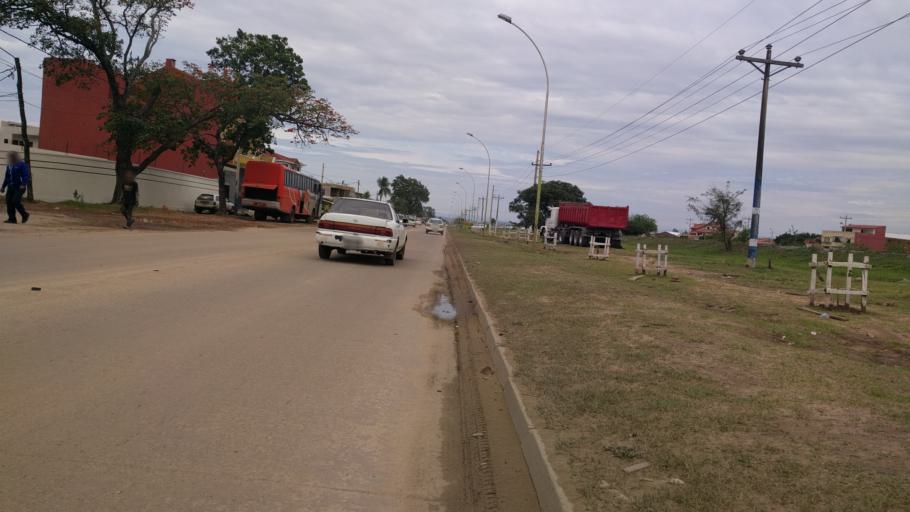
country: BO
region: Santa Cruz
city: Santa Cruz de la Sierra
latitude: -17.8438
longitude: -63.1738
